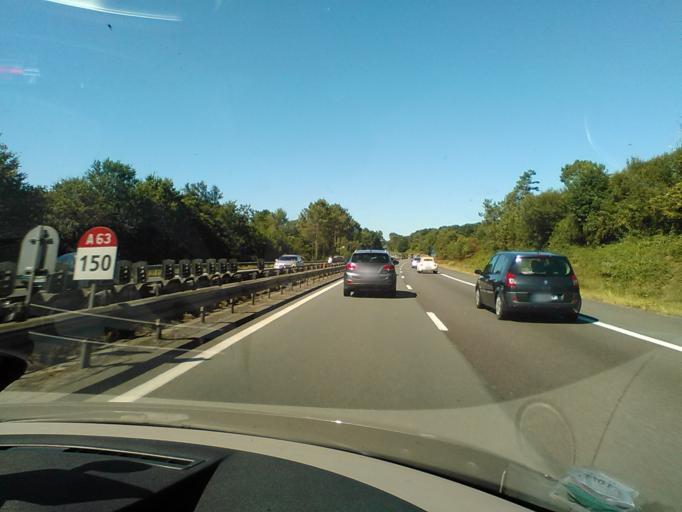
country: FR
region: Aquitaine
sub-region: Departement des Landes
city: Saubion
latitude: 43.6538
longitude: -1.3381
